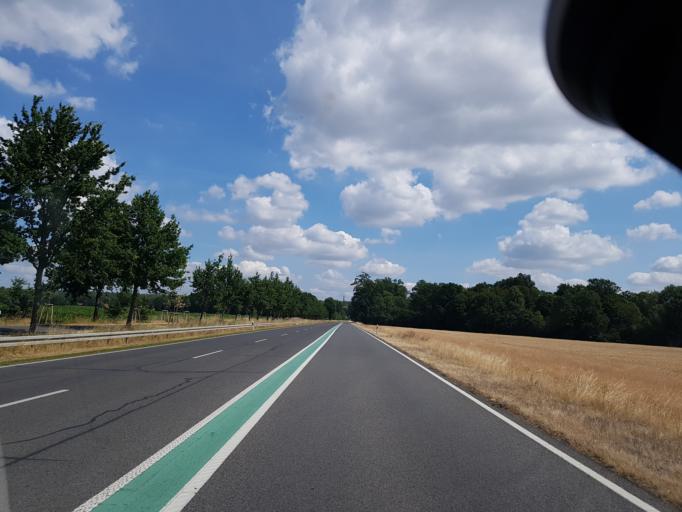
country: DE
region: Brandenburg
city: Drebkau
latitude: 51.6853
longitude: 14.2608
